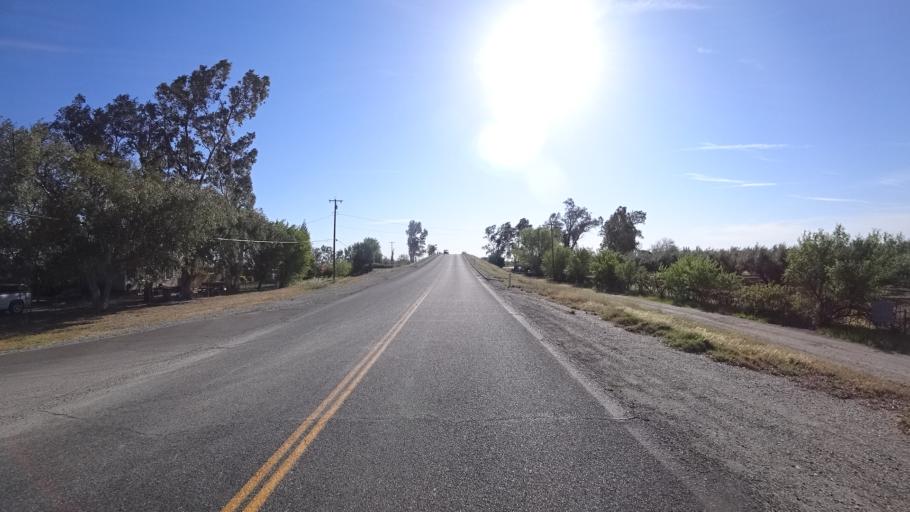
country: US
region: California
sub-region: Glenn County
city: Orland
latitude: 39.7258
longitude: -122.2080
